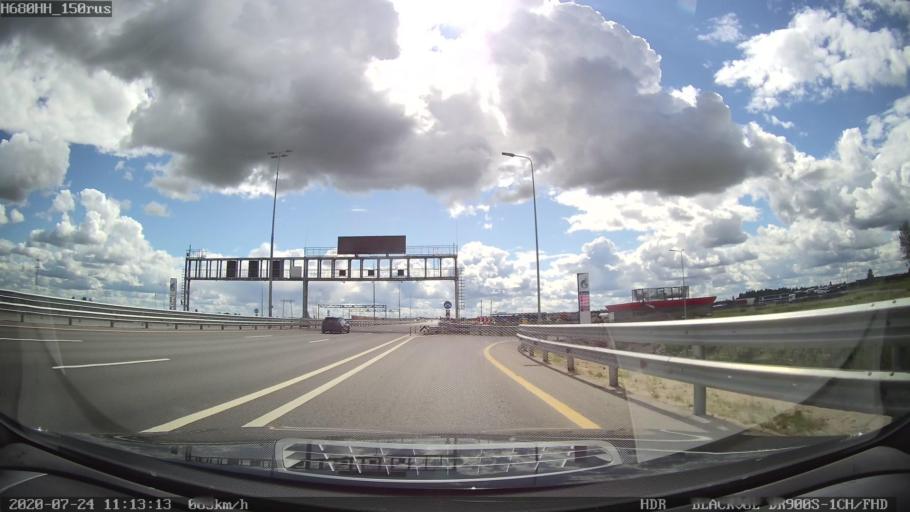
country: RU
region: Leningrad
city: Fedorovskoye
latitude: 59.7025
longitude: 30.5509
